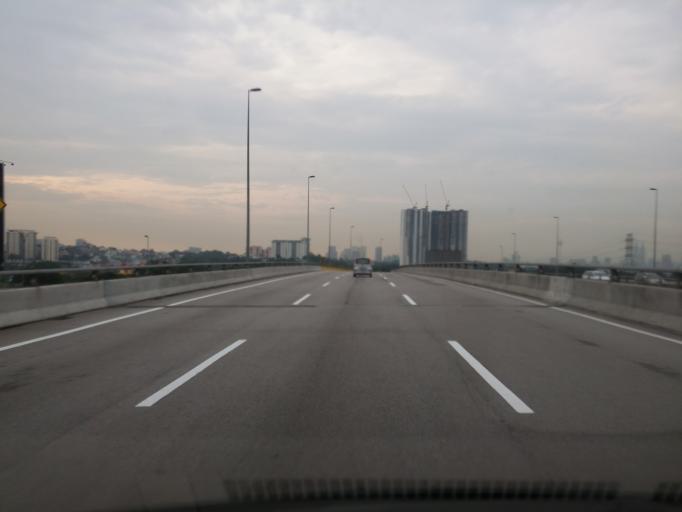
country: MY
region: Kuala Lumpur
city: Kuala Lumpur
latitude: 3.0940
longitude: 101.6958
